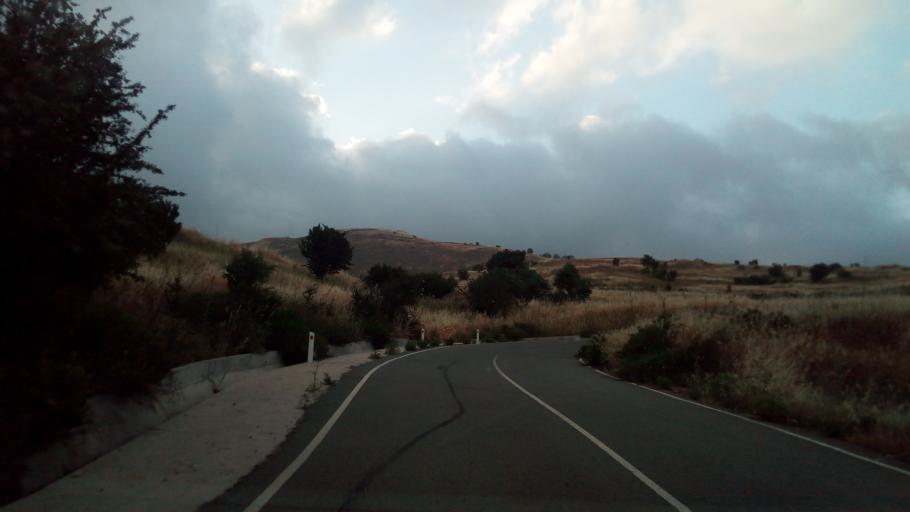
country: CY
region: Limassol
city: Pachna
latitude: 34.8674
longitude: 32.6365
